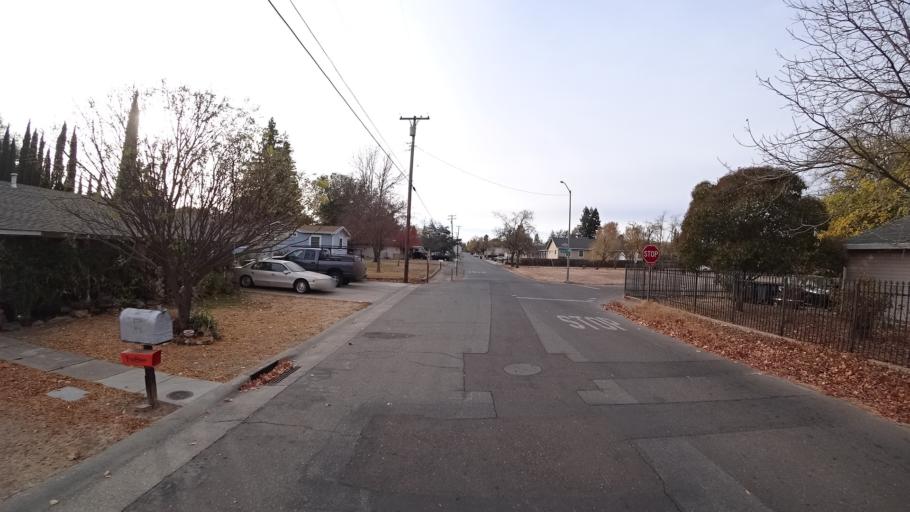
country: US
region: California
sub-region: Sacramento County
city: Citrus Heights
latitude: 38.7123
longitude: -121.2765
